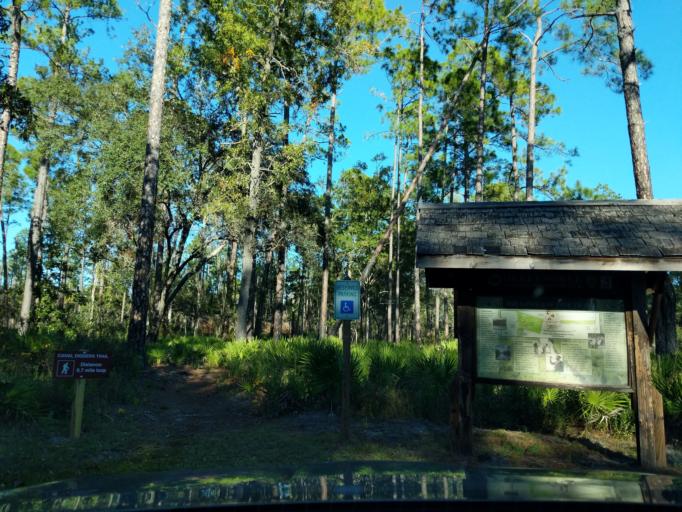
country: US
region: Georgia
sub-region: Charlton County
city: Folkston
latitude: 30.7380
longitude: -82.1368
